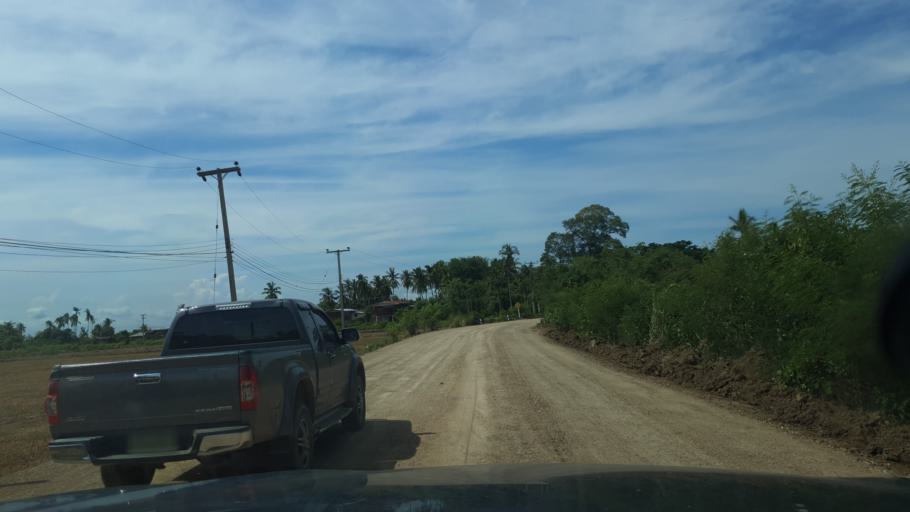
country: TH
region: Sukhothai
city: Si Samrong
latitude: 17.2097
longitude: 99.7192
